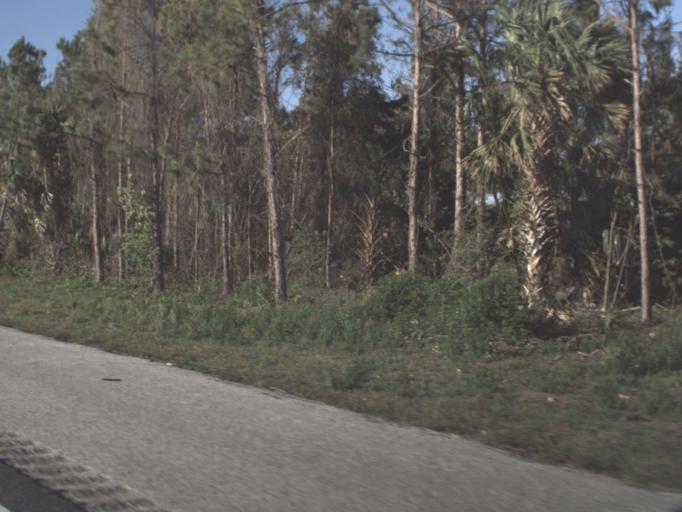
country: US
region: Florida
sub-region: Flagler County
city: Flagler Beach
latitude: 29.4517
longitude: -81.1744
